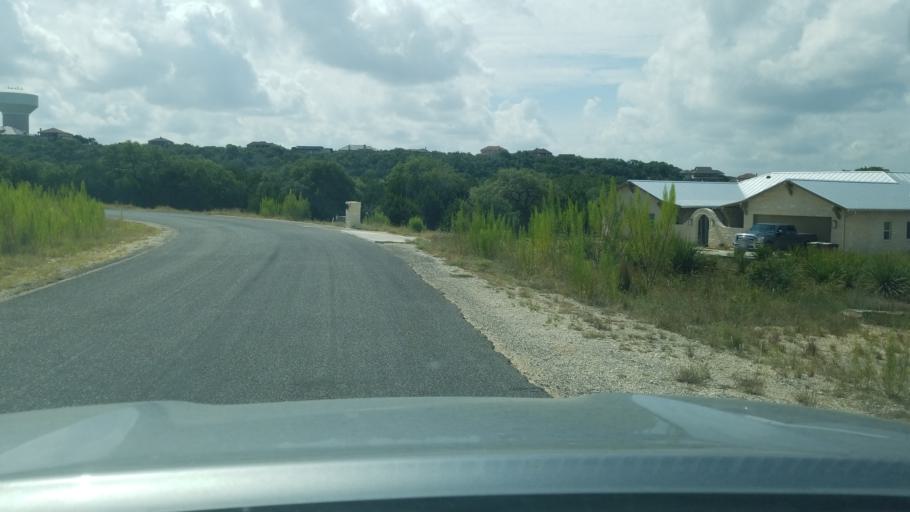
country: US
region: Texas
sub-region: Bexar County
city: Timberwood Park
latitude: 29.6840
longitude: -98.5195
